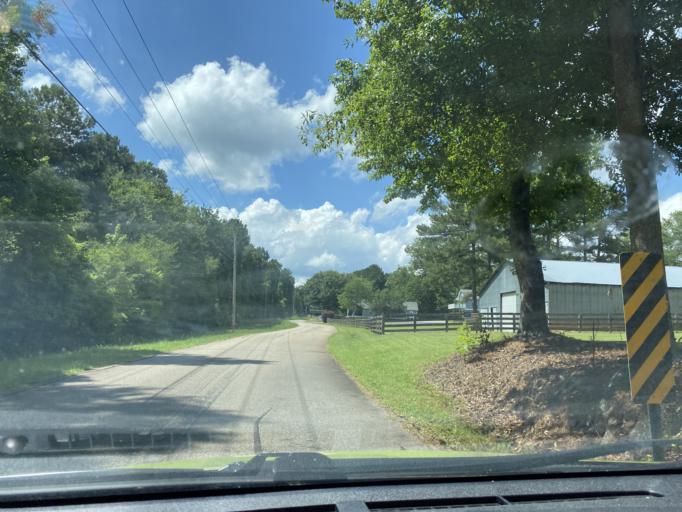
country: US
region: Georgia
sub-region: Fulton County
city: Palmetto
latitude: 33.4304
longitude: -84.7101
